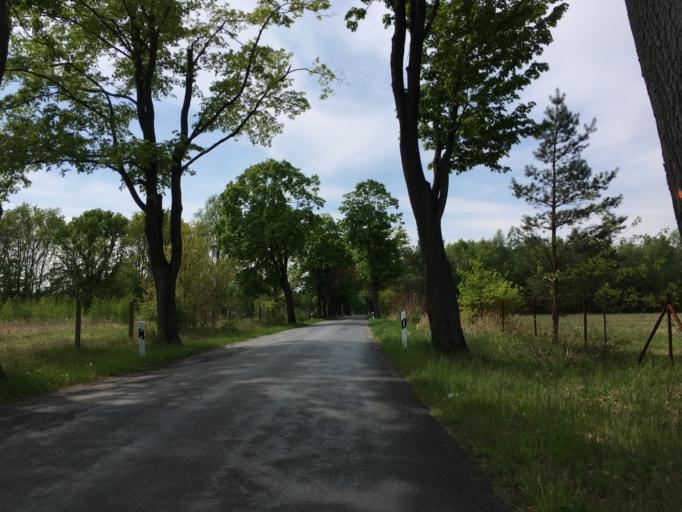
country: DE
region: Brandenburg
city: Melchow
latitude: 52.7438
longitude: 13.6828
